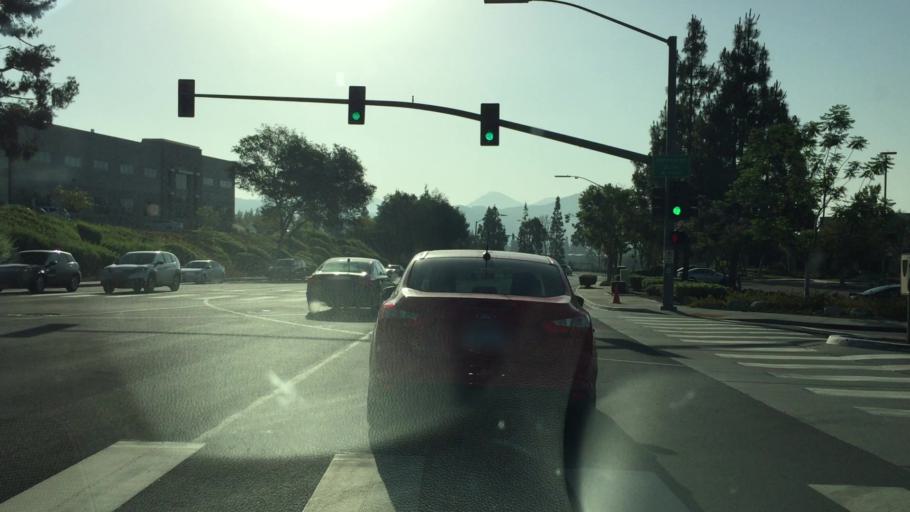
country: US
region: California
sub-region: San Diego County
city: Poway
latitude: 32.9886
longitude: -117.0771
